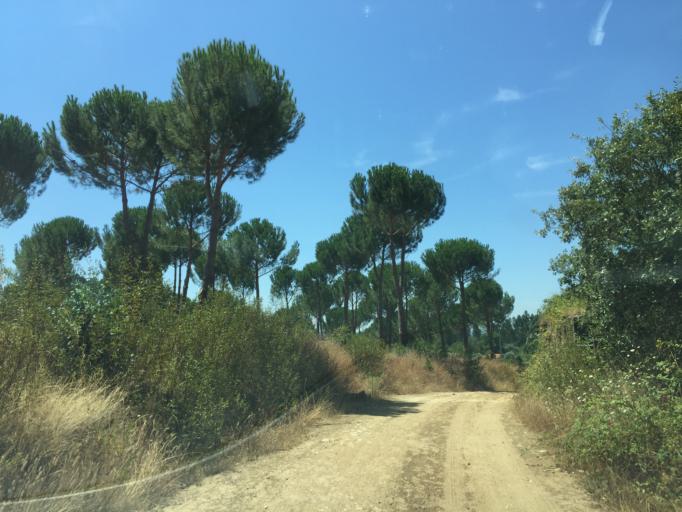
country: PT
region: Santarem
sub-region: Tomar
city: Tomar
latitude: 39.5996
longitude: -8.3567
